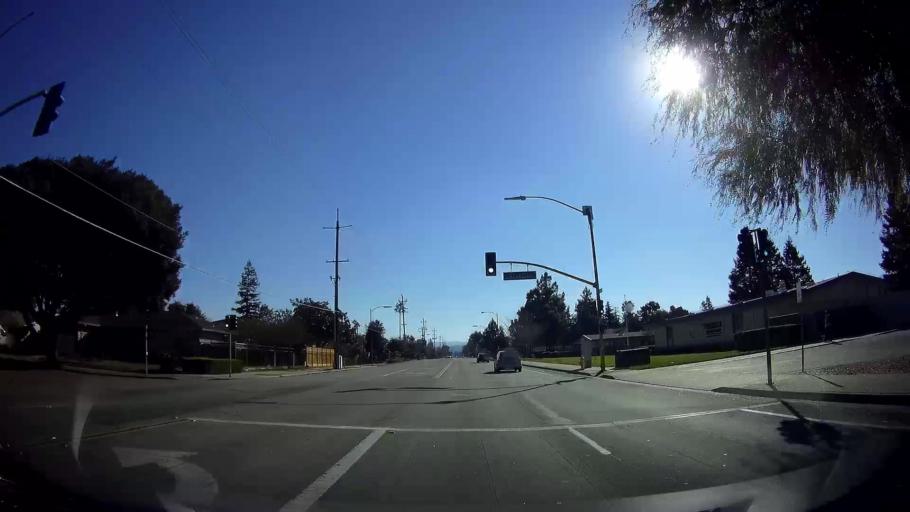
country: US
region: California
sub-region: Santa Clara County
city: Seven Trees
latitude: 37.2711
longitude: -121.8685
